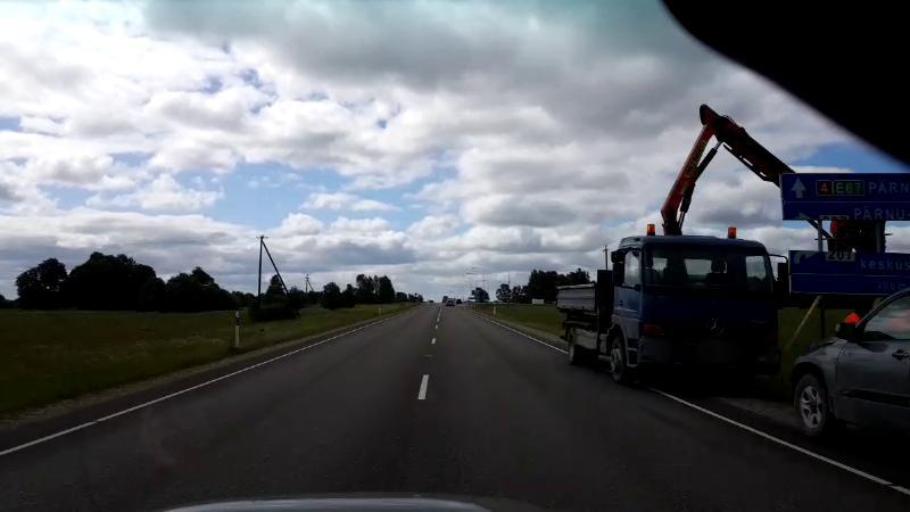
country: EE
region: Paernumaa
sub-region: Halinga vald
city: Parnu-Jaagupi
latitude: 58.5953
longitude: 24.5122
